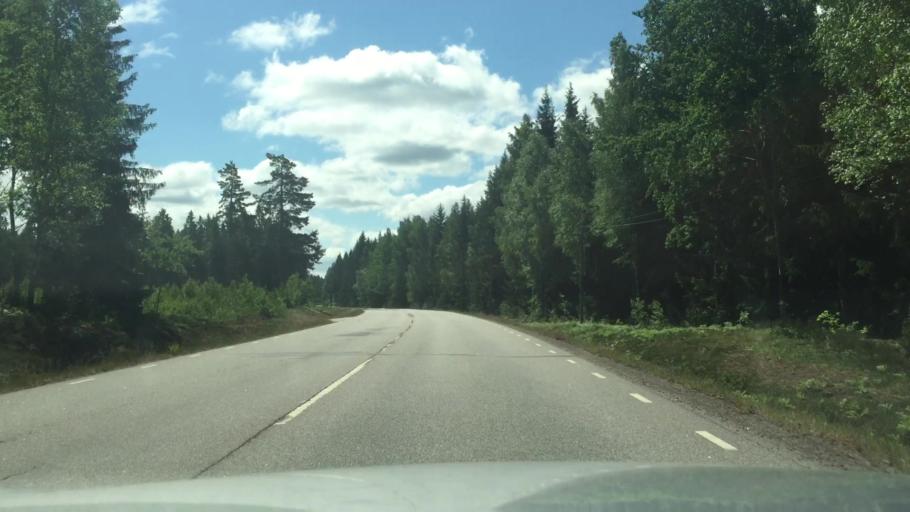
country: SE
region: Vaestra Goetaland
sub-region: Karlsborgs Kommun
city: Molltorp
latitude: 58.6206
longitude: 14.3880
